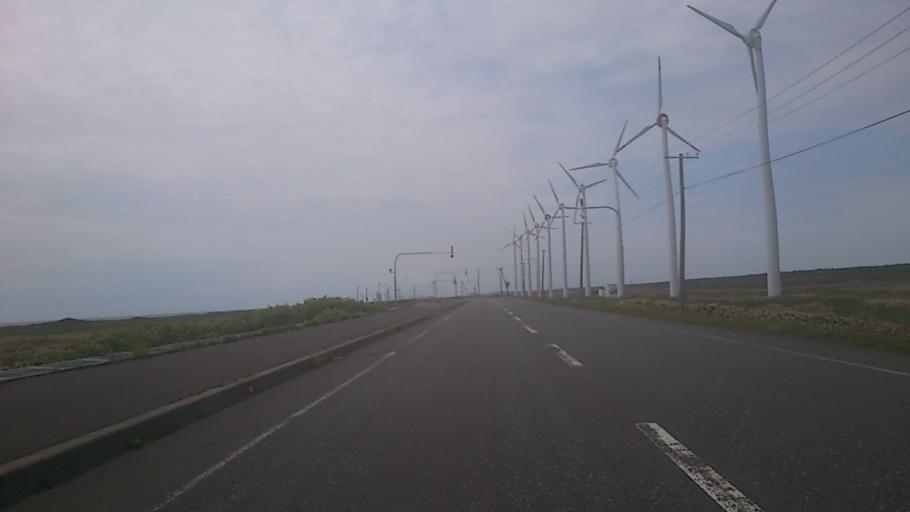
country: JP
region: Hokkaido
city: Makubetsu
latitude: 44.9716
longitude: 141.6991
